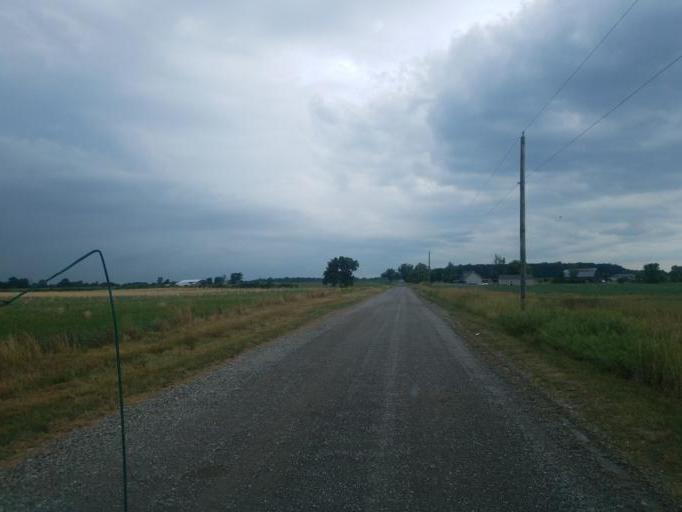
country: US
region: Ohio
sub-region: Defiance County
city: Hicksville
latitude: 41.3203
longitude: -84.8039
